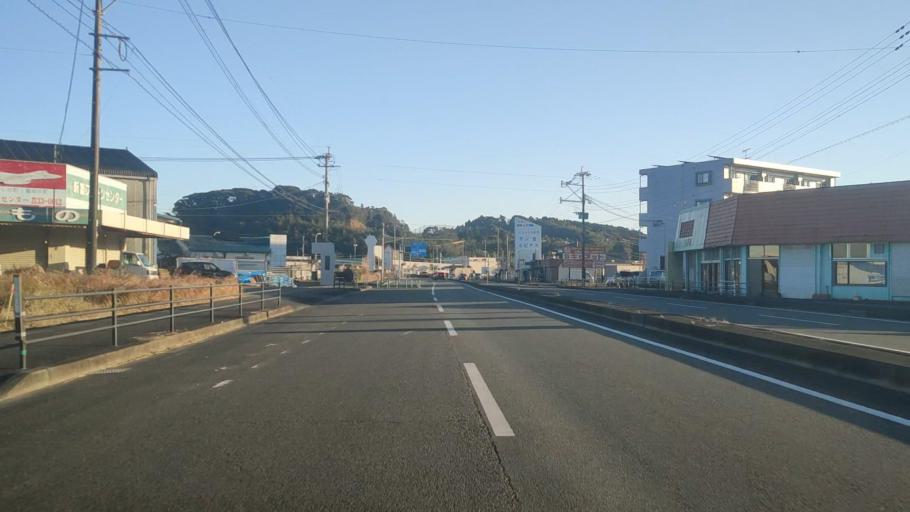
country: JP
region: Miyazaki
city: Takanabe
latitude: 32.0729
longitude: 131.4938
